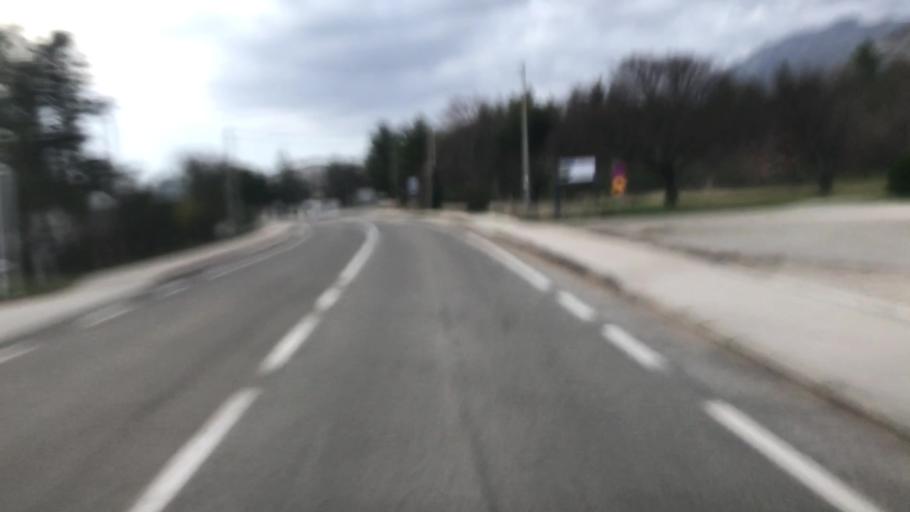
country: HR
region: Zadarska
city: Starigrad
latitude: 44.2879
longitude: 15.4486
